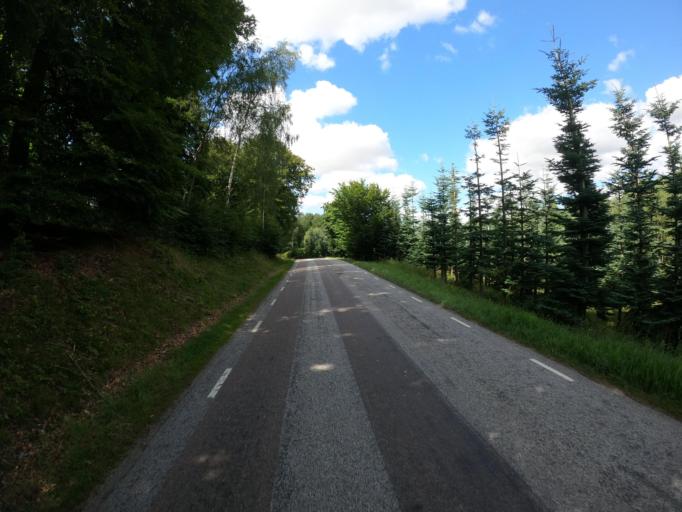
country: SE
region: Skane
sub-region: Lunds Kommun
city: Genarp
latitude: 55.5882
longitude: 13.4411
